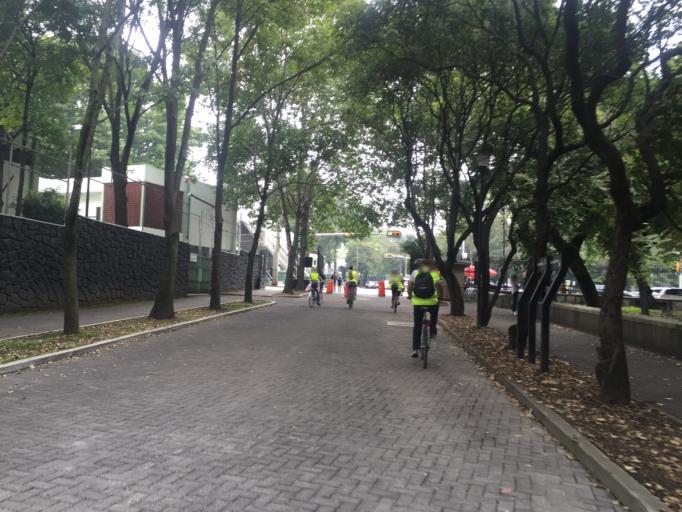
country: MX
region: Mexico City
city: Polanco
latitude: 19.4211
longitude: -99.1919
